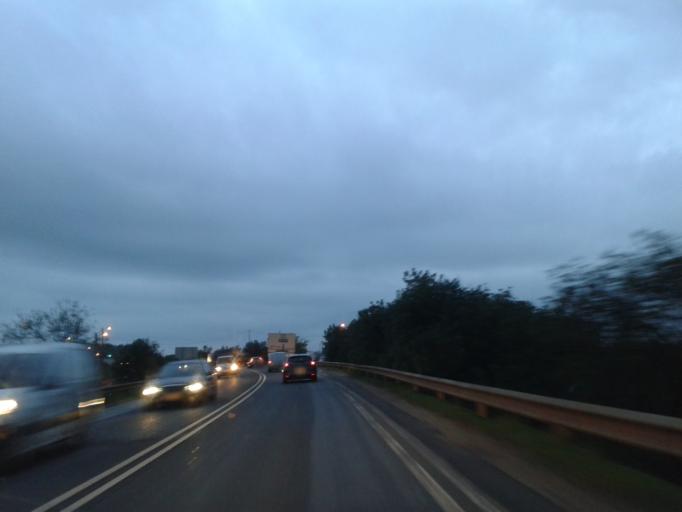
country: PT
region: Faro
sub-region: Albufeira
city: Ferreiras
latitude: 37.1241
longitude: -8.2196
